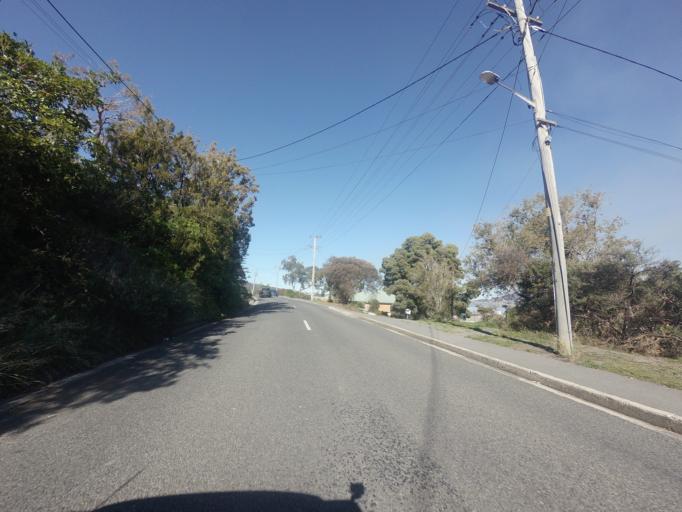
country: AU
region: Tasmania
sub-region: Clarence
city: Lindisfarne
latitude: -42.8452
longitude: 147.3394
